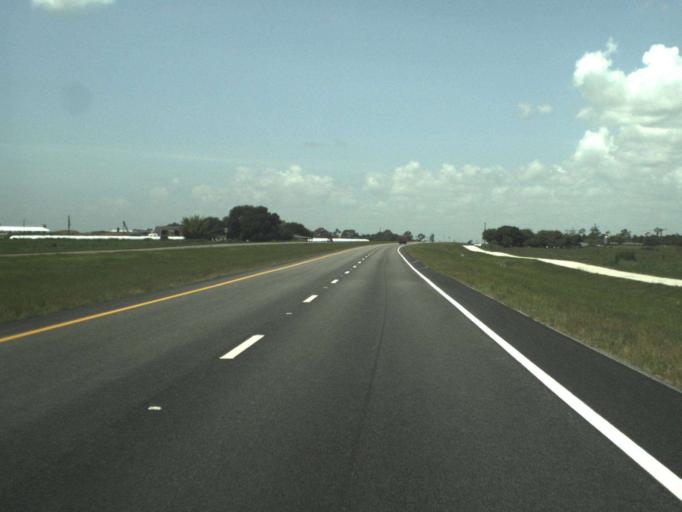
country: US
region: Florida
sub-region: Okeechobee County
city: Taylor Creek
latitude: 27.3070
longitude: -80.6696
